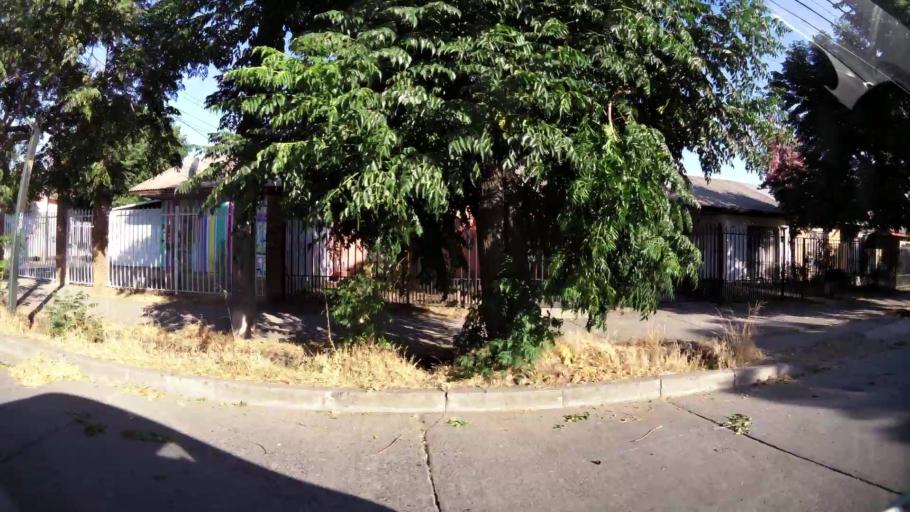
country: CL
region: Maule
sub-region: Provincia de Talca
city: Talca
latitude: -35.4375
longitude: -71.6907
